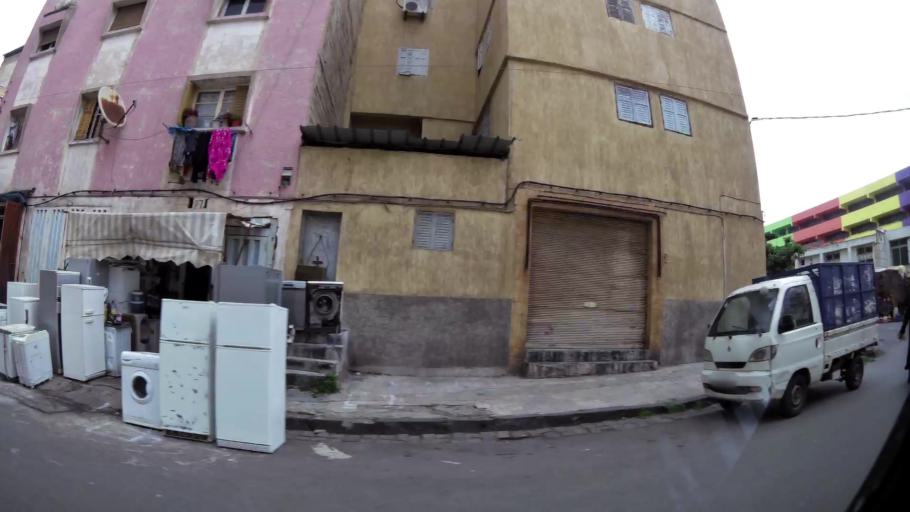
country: MA
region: Grand Casablanca
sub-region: Casablanca
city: Casablanca
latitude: 33.5863
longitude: -7.5601
